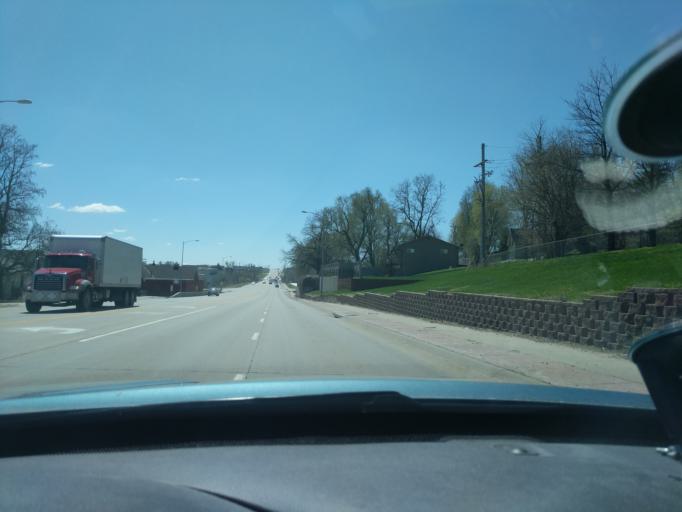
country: US
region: Nebraska
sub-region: Douglas County
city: Elkhorn
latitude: 41.2851
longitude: -96.2345
